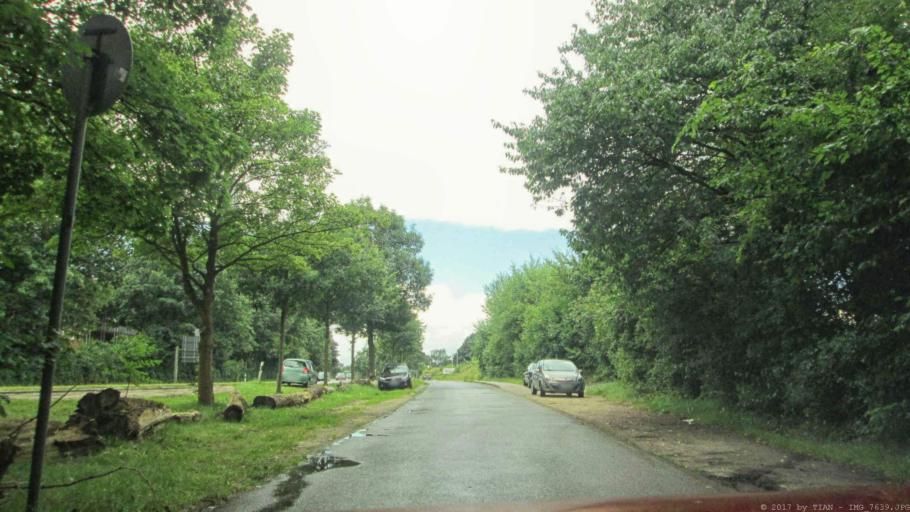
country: DE
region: Schleswig-Holstein
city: Oststeinbek
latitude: 53.5464
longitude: 10.1424
